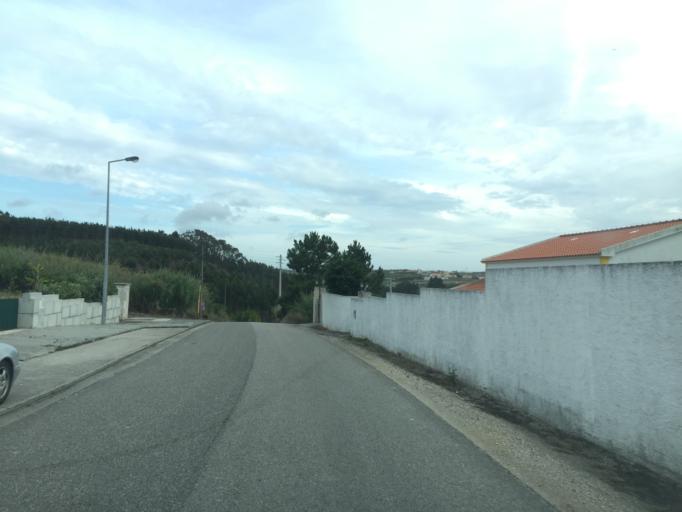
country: PT
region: Leiria
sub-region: Peniche
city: Atouguia da Baleia
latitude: 39.3493
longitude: -9.2941
